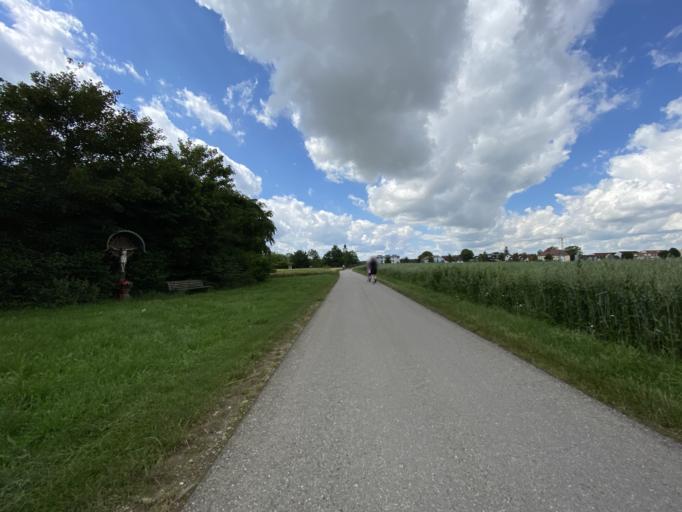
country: DE
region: Bavaria
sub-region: Upper Bavaria
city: Gilching
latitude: 48.1065
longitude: 11.3120
